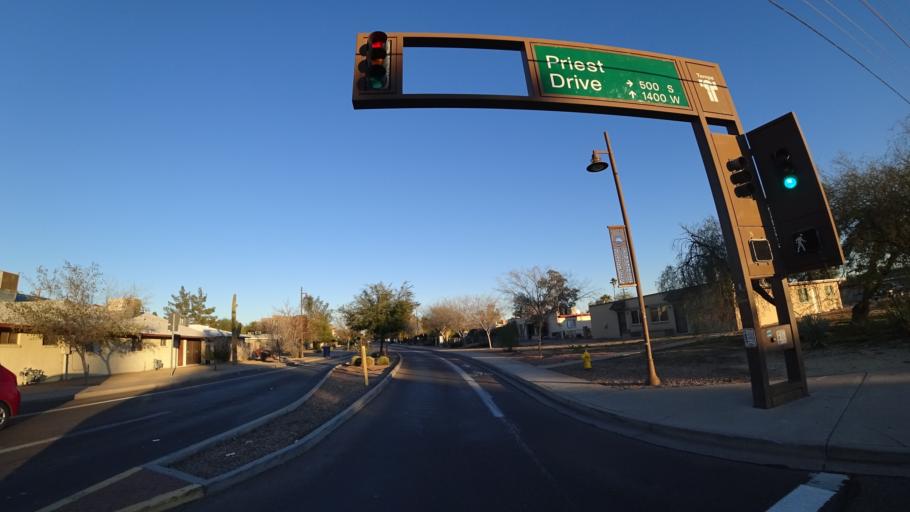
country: US
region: Arizona
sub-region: Maricopa County
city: Tempe Junction
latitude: 33.4255
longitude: -111.9609
